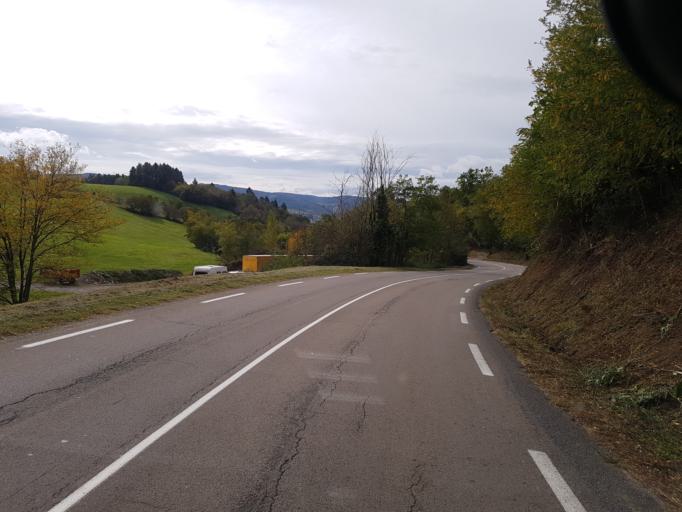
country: FR
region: Rhone-Alpes
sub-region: Departement de la Loire
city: Unieux
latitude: 45.4083
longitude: 4.2947
